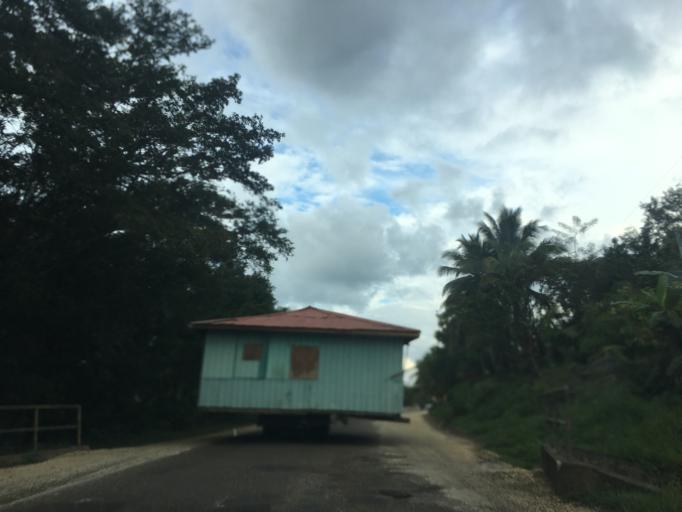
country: BZ
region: Cayo
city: San Ignacio
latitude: 17.2069
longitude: -88.9437
